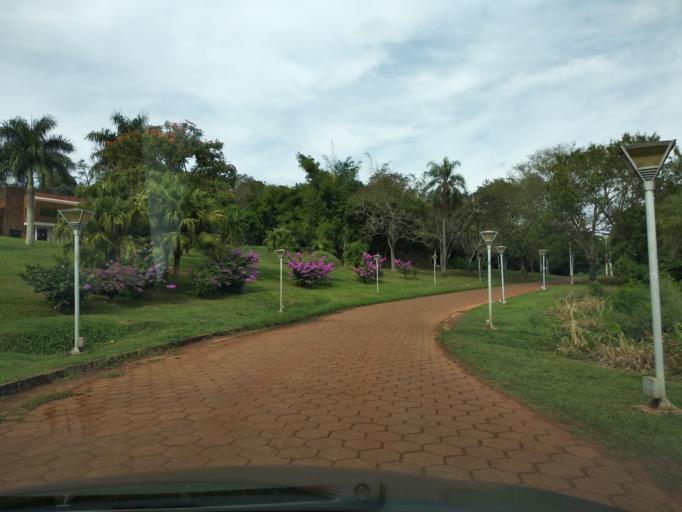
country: AR
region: Misiones
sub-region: Departamento de Iguazu
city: Puerto Iguazu
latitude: -25.5935
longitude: -54.5767
